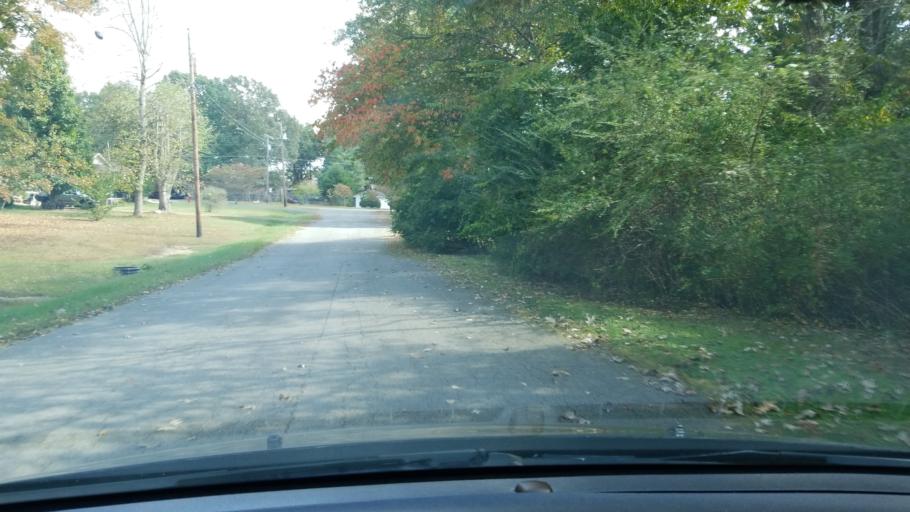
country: US
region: Tennessee
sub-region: Cumberland County
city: Crossville
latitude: 35.9626
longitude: -85.0689
